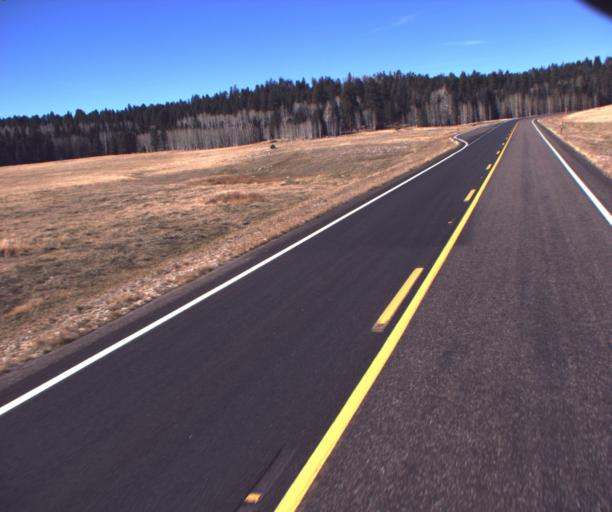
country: US
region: Arizona
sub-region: Coconino County
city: Grand Canyon
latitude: 36.5024
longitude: -112.1387
